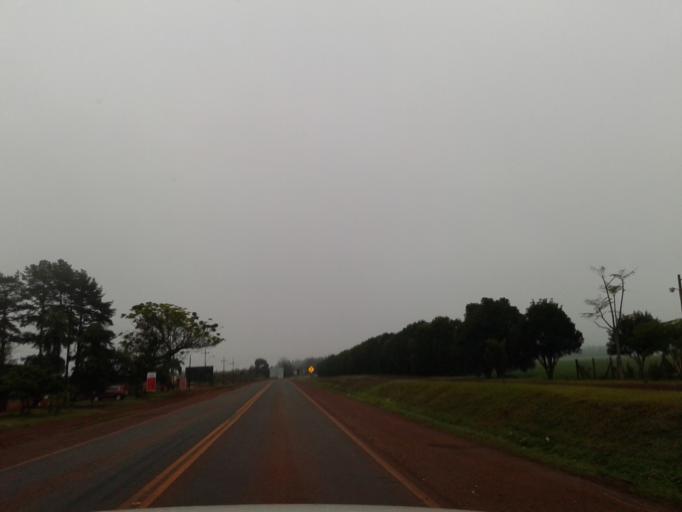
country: PY
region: Itapua
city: Pirapo
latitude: -26.8843
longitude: -55.4714
